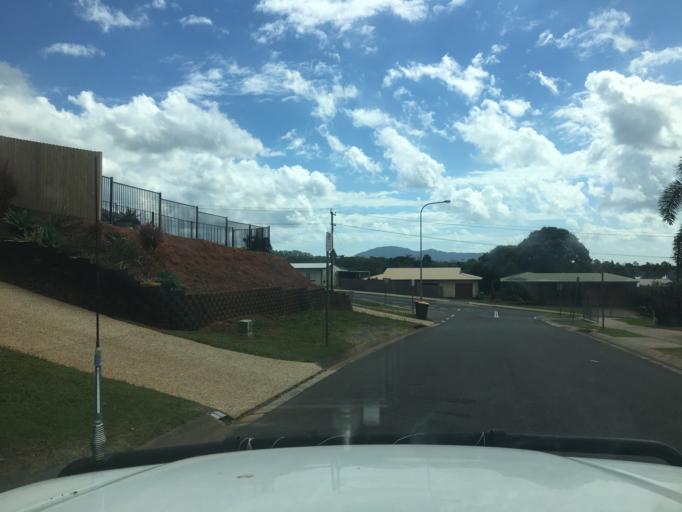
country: AU
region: Queensland
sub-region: Cairns
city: Woree
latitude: -16.9678
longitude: 145.7394
